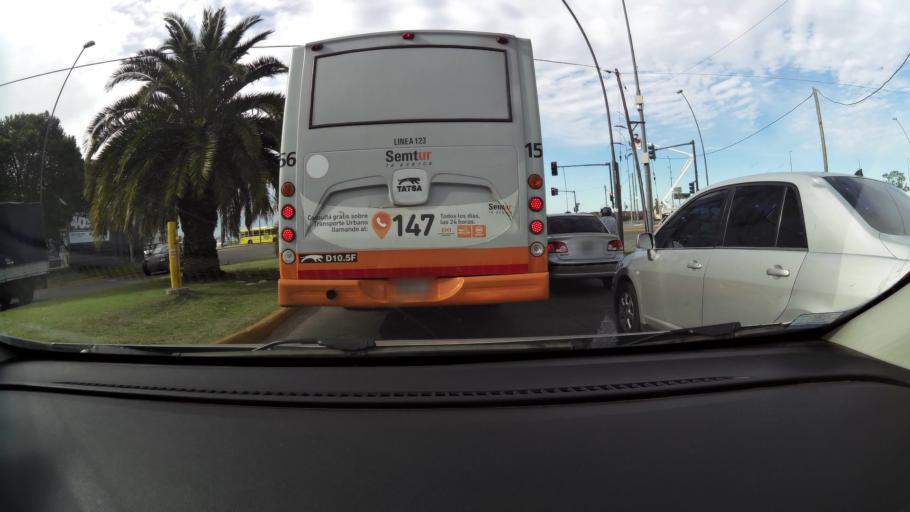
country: AR
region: Santa Fe
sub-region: Departamento de Rosario
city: Rosario
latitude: -32.9258
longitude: -60.6615
